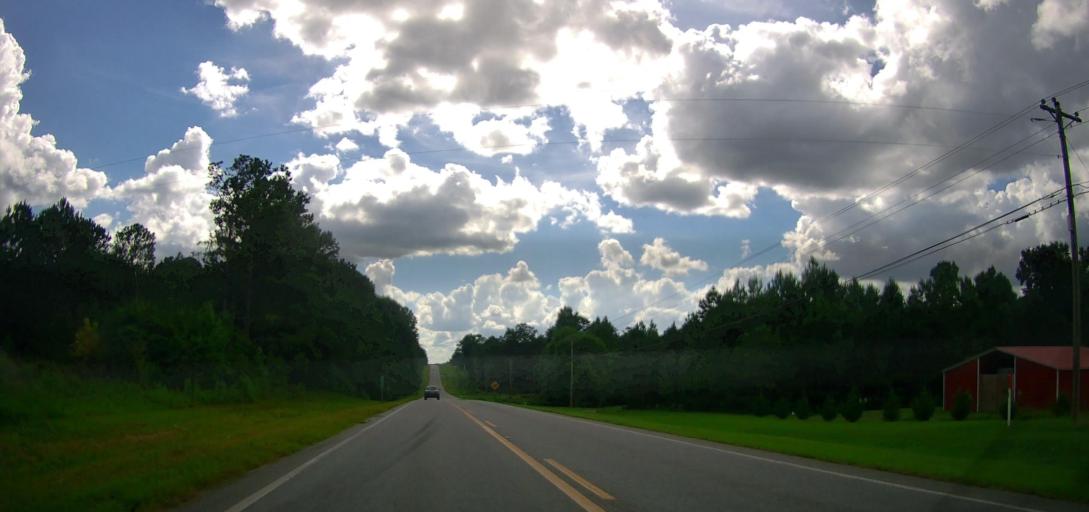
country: US
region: Alabama
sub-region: Russell County
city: Ladonia
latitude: 32.4454
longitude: -85.2700
